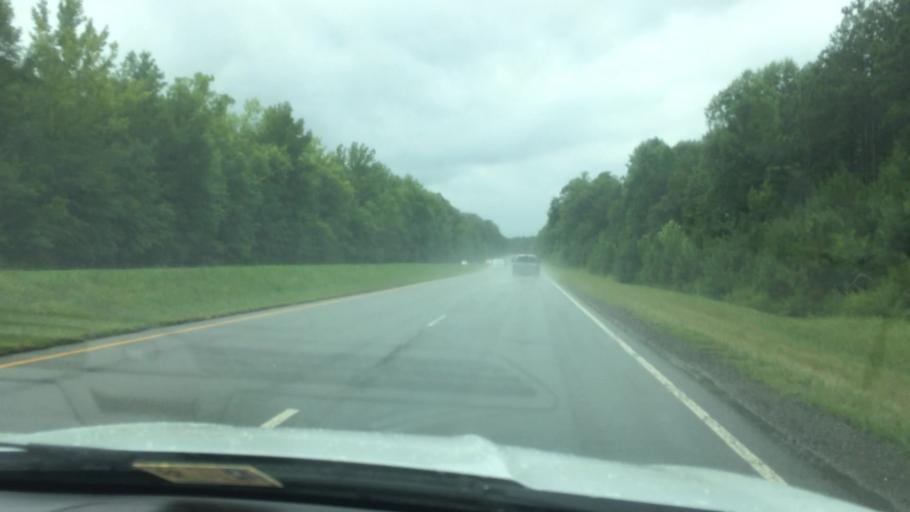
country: US
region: Virginia
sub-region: New Kent County
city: New Kent
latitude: 37.4966
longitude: -76.8868
